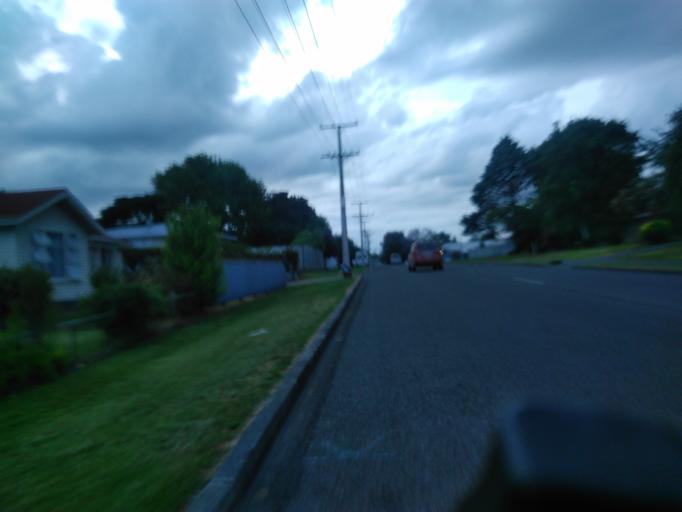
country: NZ
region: Gisborne
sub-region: Gisborne District
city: Gisborne
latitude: -38.6457
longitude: 178.0090
